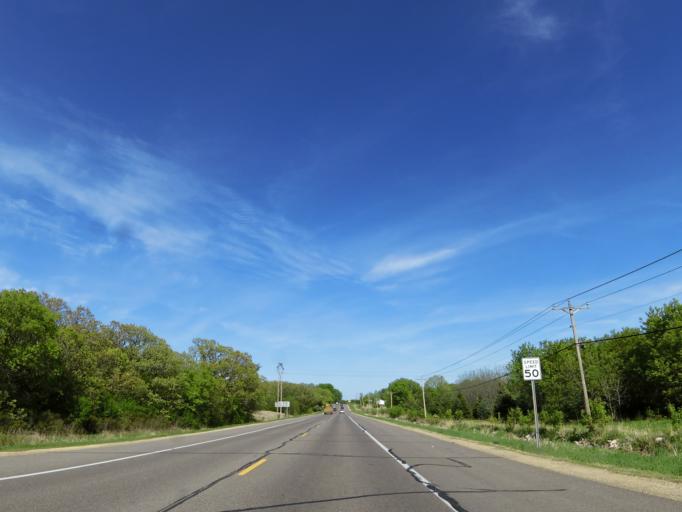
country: US
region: Minnesota
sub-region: Washington County
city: Oakdale
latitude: 44.9915
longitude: -92.9424
